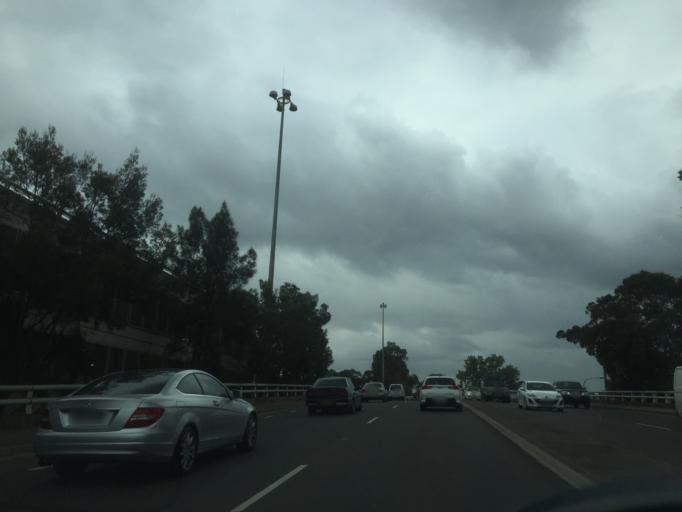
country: AU
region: New South Wales
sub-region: Blacktown
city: Blacktown
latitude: -33.7735
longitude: 150.9359
